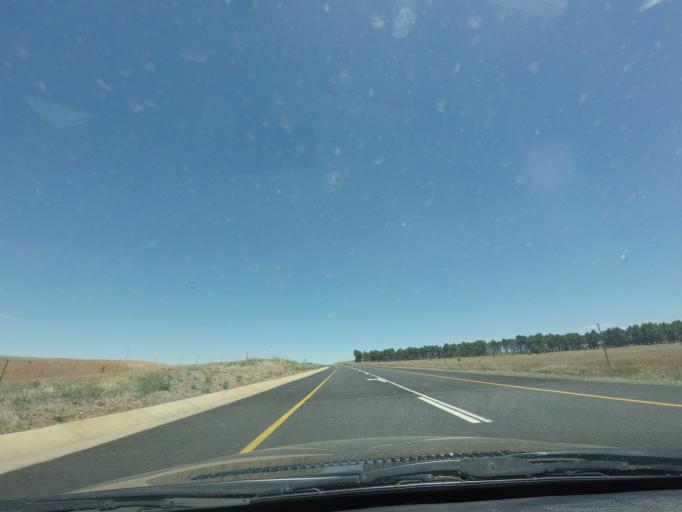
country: ZA
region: Orange Free State
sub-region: Thabo Mofutsanyana District Municipality
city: Ladybrand
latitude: -29.1792
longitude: 27.2140
